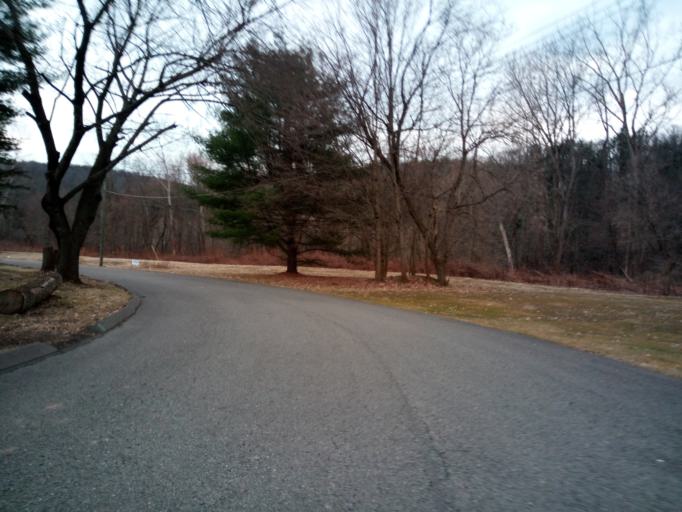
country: US
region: New York
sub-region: Chemung County
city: West Elmira
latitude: 42.0768
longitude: -76.8555
